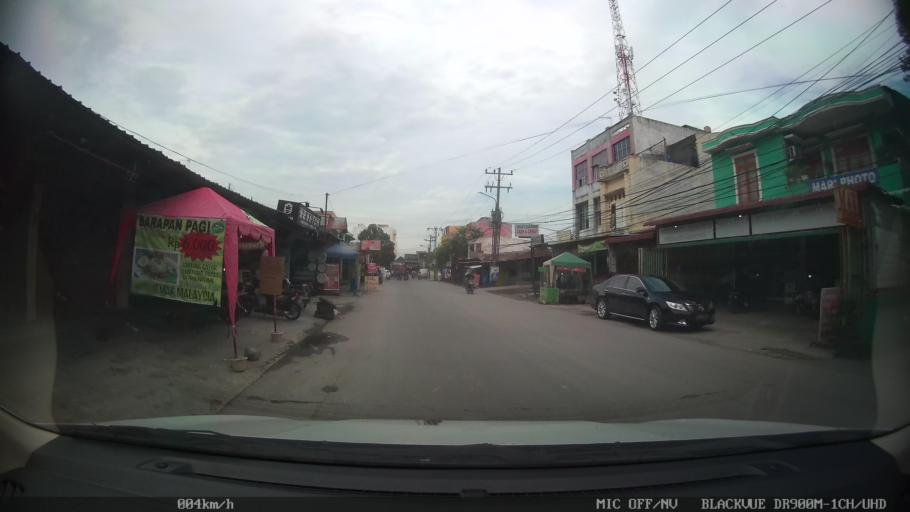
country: ID
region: North Sumatra
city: Sunggal
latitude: 3.6089
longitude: 98.6094
